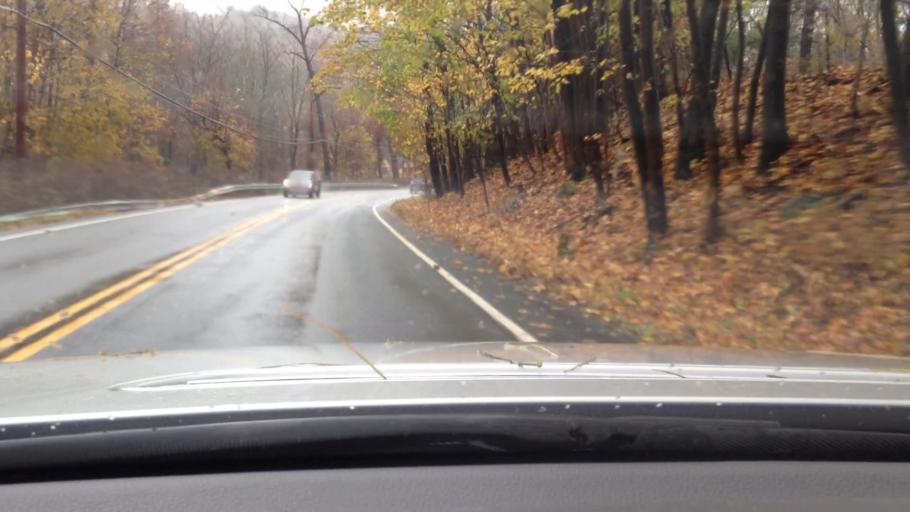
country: US
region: New York
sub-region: Putnam County
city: Cold Spring
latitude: 41.4178
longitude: -73.9411
